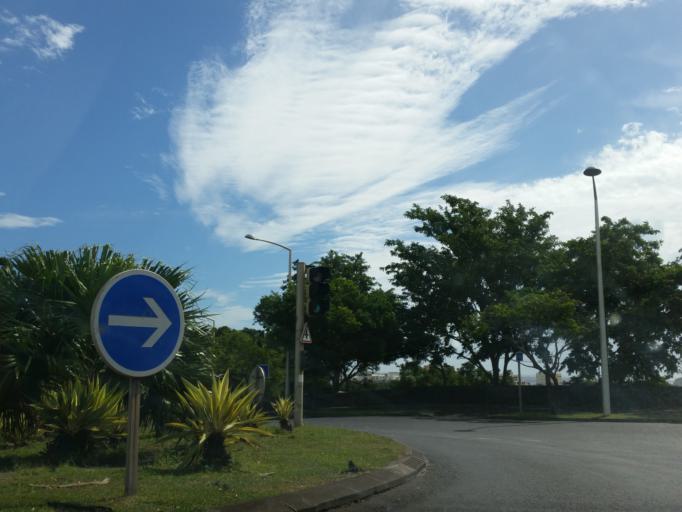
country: RE
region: Reunion
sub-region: Reunion
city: Saint-Denis
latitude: -20.8935
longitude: 55.4707
